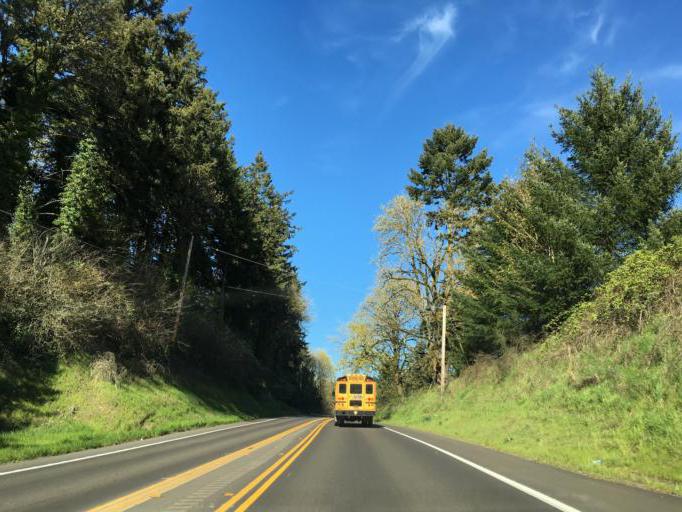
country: US
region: Oregon
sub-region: Clackamas County
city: Canby
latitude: 45.2351
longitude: -122.7454
